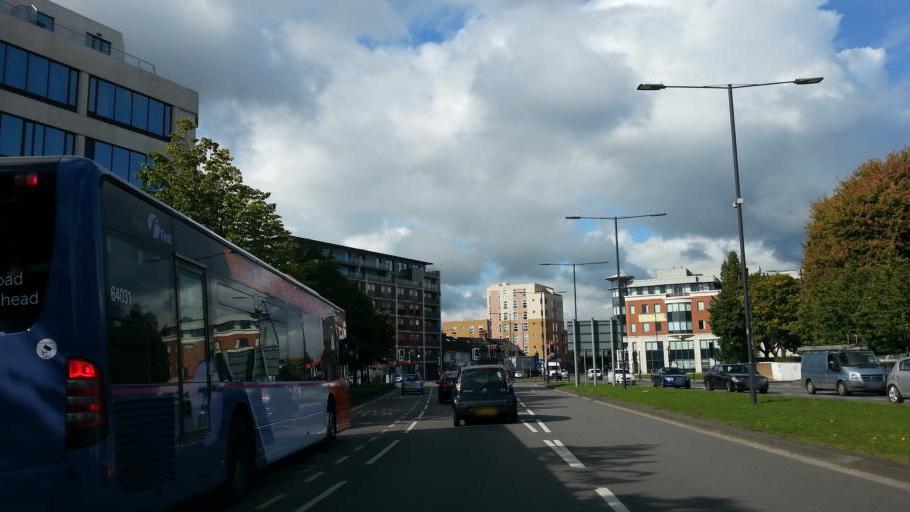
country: GB
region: England
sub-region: Slough
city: Slough
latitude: 51.5105
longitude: -0.5960
